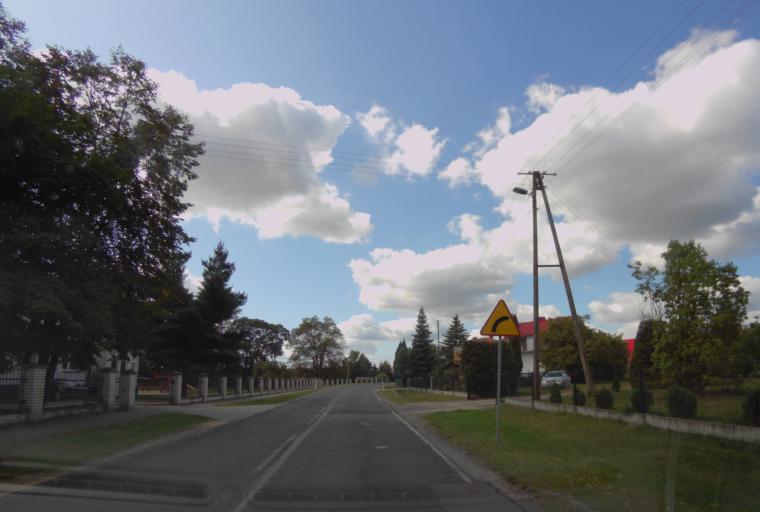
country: PL
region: Subcarpathian Voivodeship
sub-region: Powiat stalowowolski
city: Bojanow
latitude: 50.4243
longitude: 21.9482
